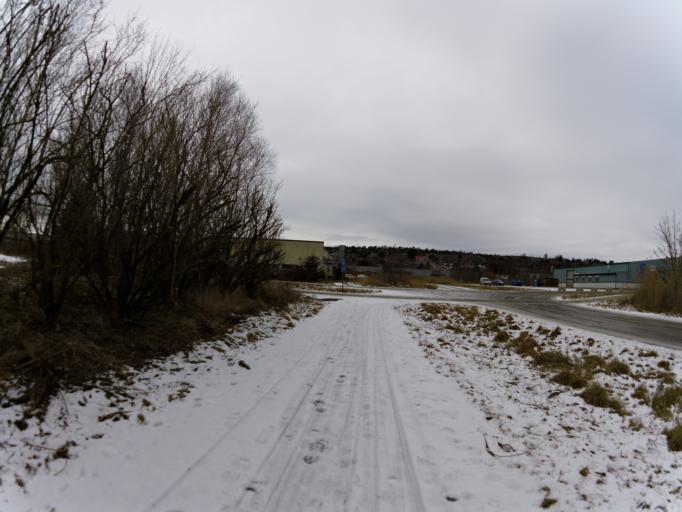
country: NO
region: Ostfold
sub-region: Fredrikstad
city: Fredrikstad
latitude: 59.2087
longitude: 10.8917
